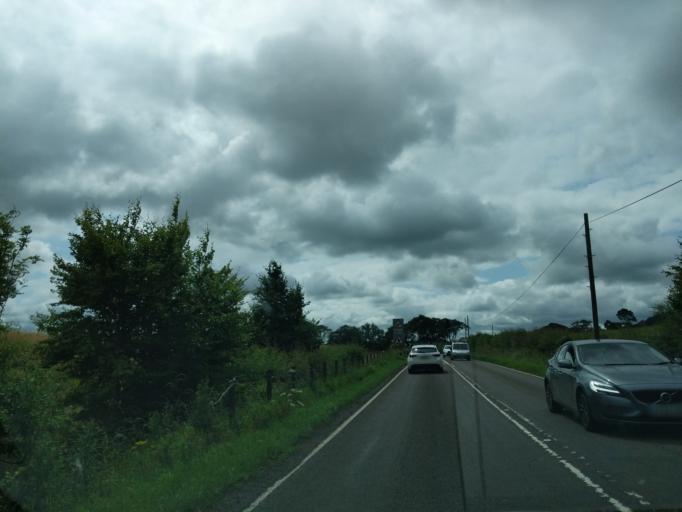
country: GB
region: Scotland
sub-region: South Lanarkshire
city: Strathaven
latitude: 55.6792
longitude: -4.0431
